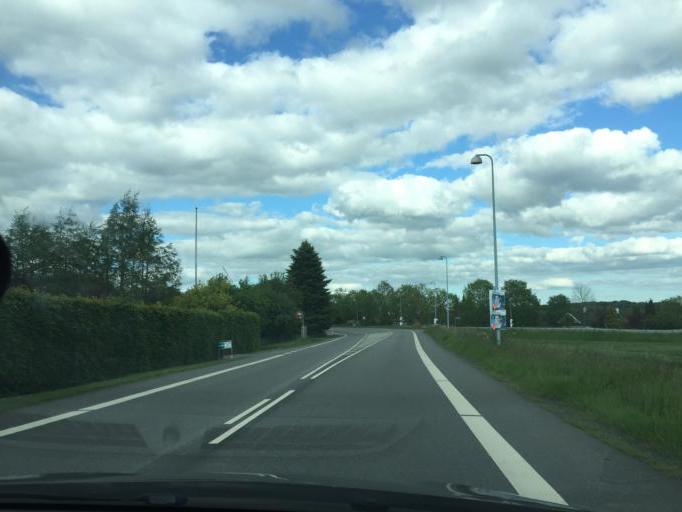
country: DK
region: South Denmark
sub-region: Odense Kommune
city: Bellinge
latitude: 55.3460
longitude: 10.3325
